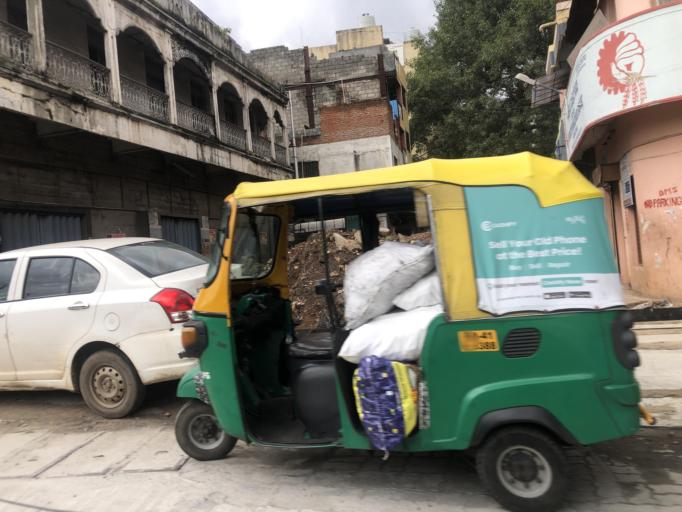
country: IN
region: Karnataka
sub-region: Bangalore Urban
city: Bangalore
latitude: 12.9730
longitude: 77.5691
